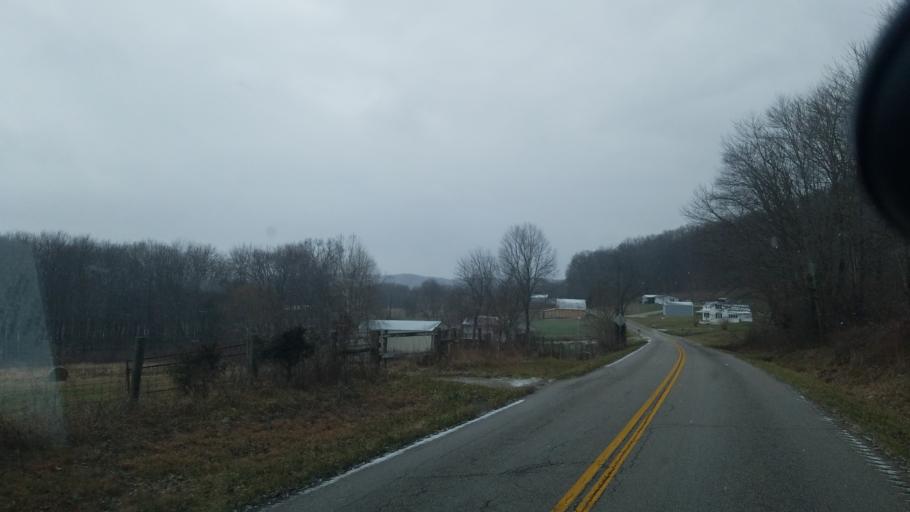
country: US
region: Kentucky
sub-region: Fleming County
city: Flemingsburg
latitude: 38.4687
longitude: -83.5574
